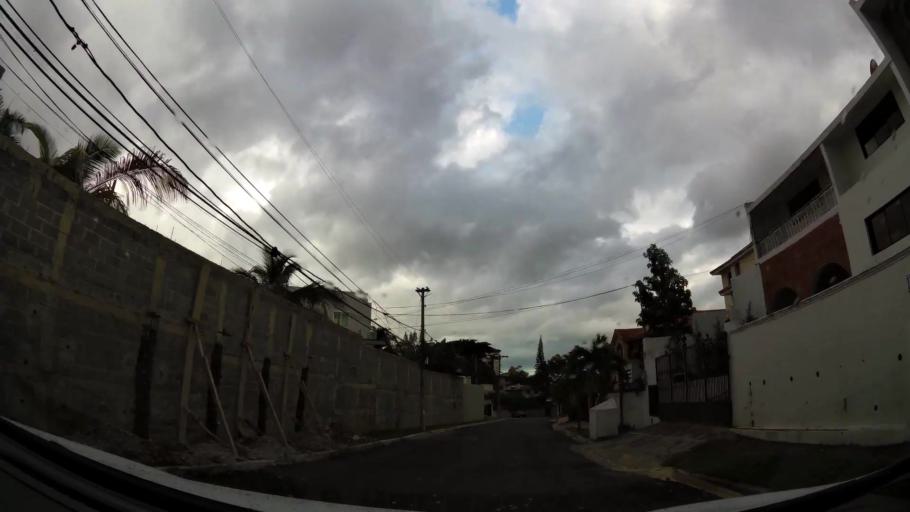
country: DO
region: Nacional
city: Santo Domingo
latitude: 18.5052
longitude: -69.9674
